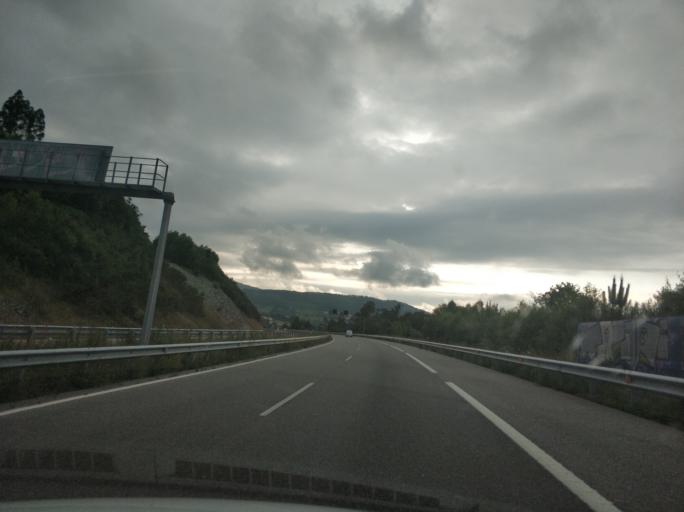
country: ES
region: Asturias
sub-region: Province of Asturias
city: Cudillero
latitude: 43.5444
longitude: -6.1361
